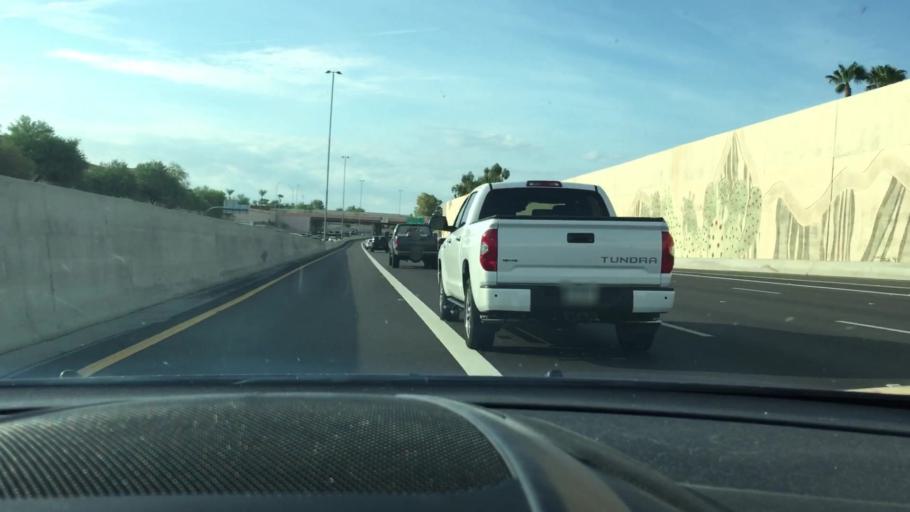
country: US
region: Arizona
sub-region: Maricopa County
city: Scottsdale
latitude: 33.5779
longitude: -111.8909
